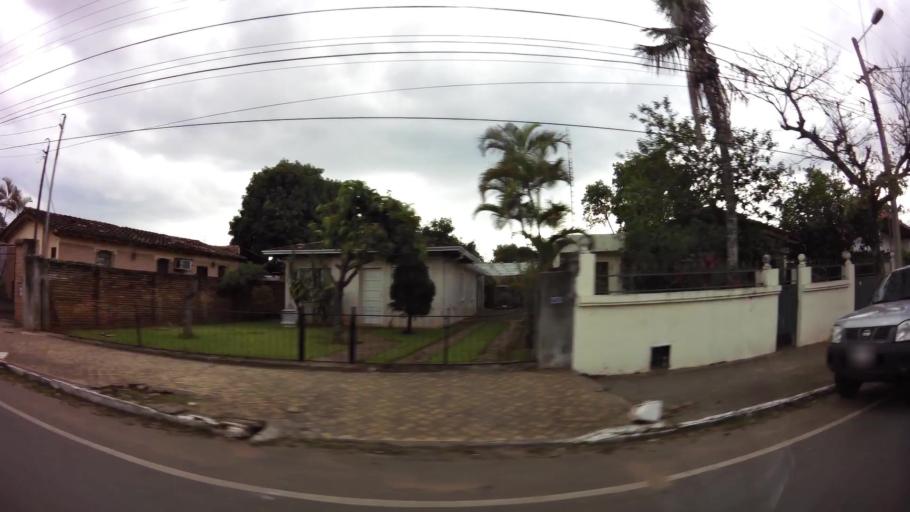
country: PY
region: Central
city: Fernando de la Mora
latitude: -25.3314
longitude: -57.5556
